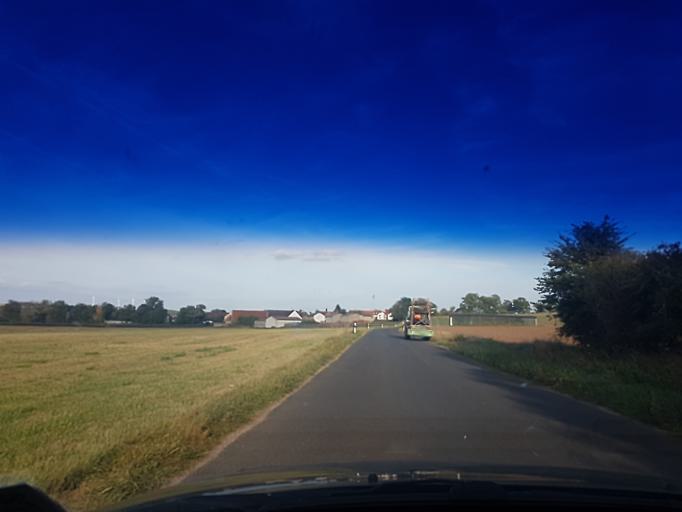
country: DE
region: Bavaria
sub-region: Regierungsbezirk Mittelfranken
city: Wachenroth
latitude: 49.7437
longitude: 10.6847
